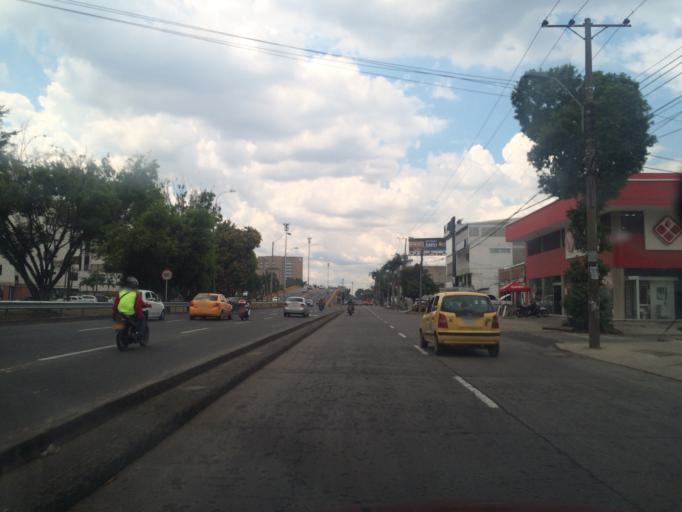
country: CO
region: Valle del Cauca
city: Cali
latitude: 3.4038
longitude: -76.5406
